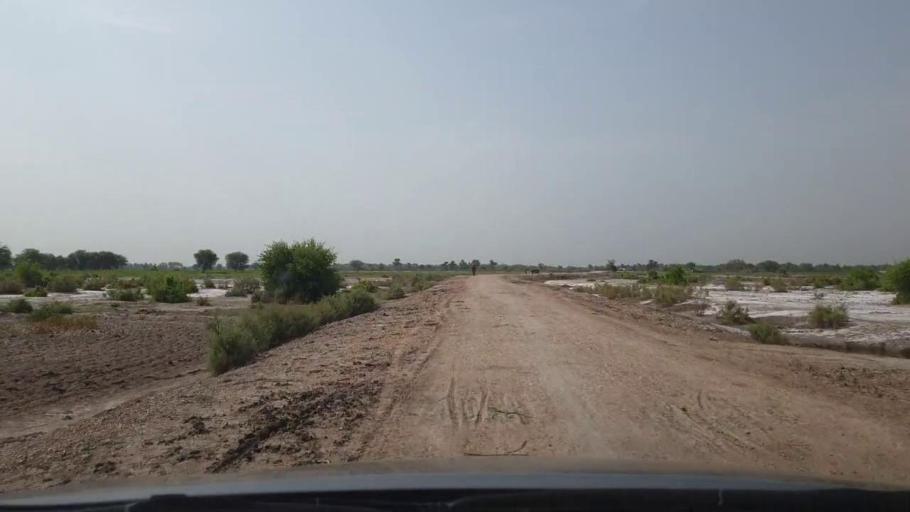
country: PK
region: Sindh
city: Rohri
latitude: 27.6698
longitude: 69.0135
